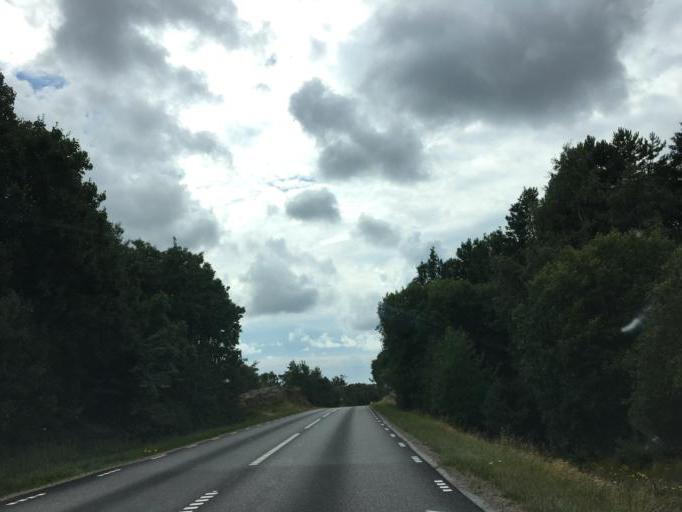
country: SE
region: Vaestra Goetaland
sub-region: Sotenas Kommun
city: Hunnebostrand
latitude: 58.4101
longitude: 11.2748
